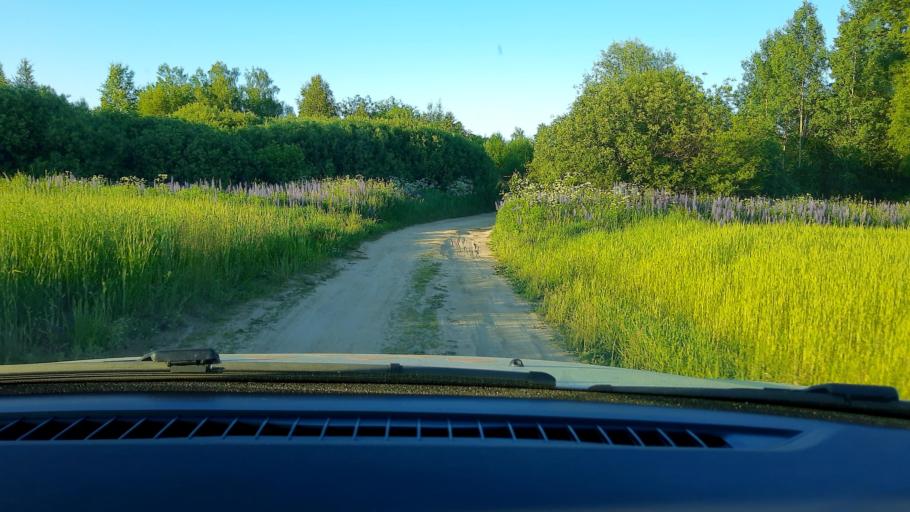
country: RU
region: Nizjnij Novgorod
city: Kstovo
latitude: 56.3081
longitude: 44.2686
